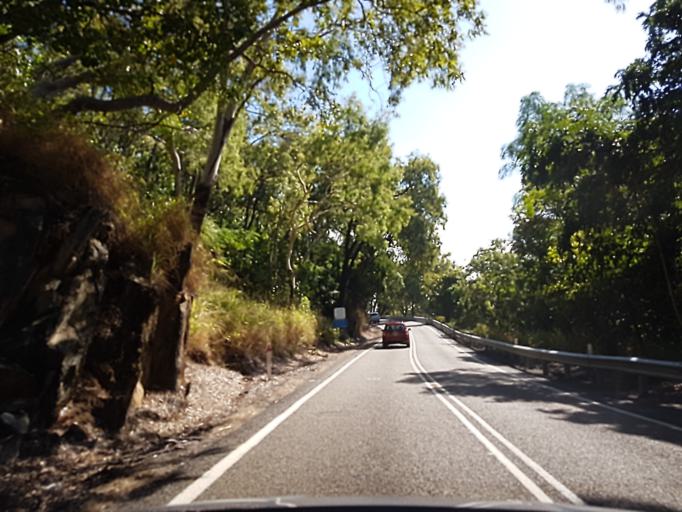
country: AU
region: Queensland
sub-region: Cairns
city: Port Douglas
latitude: -16.6077
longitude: 145.5282
